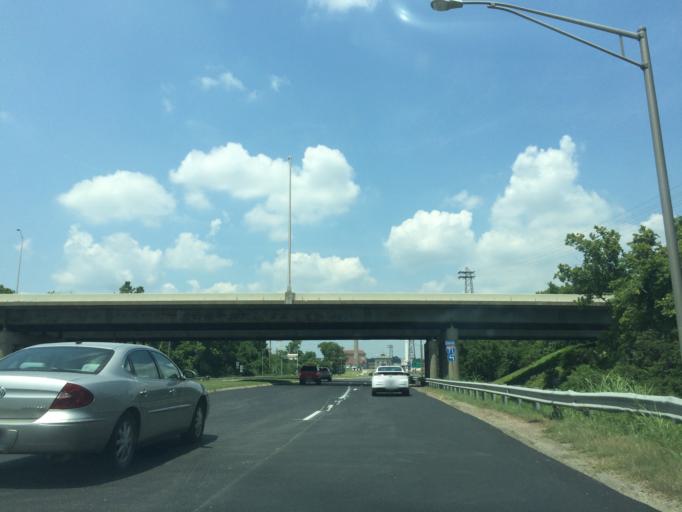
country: US
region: Indiana
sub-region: Clark County
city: Oak Park
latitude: 38.2744
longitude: -85.6967
